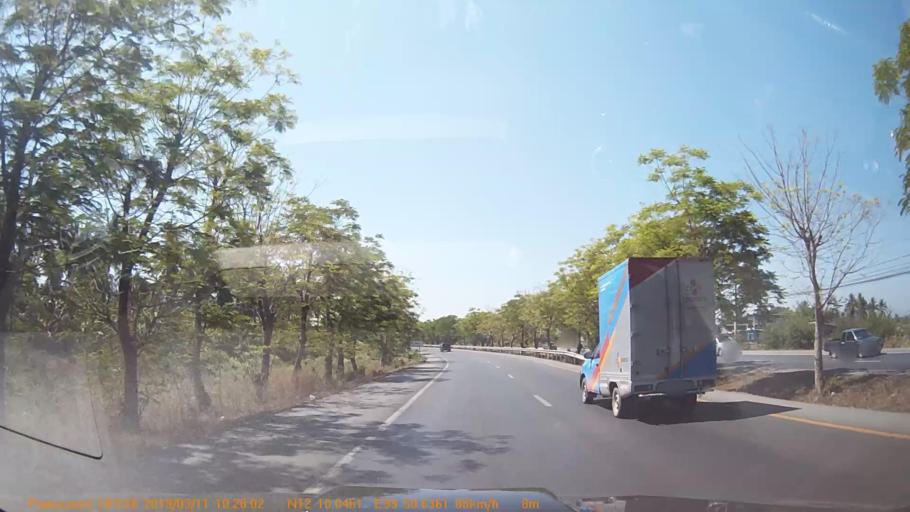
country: TH
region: Prachuap Khiri Khan
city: Kui Buri
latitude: 12.1672
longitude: 99.8439
